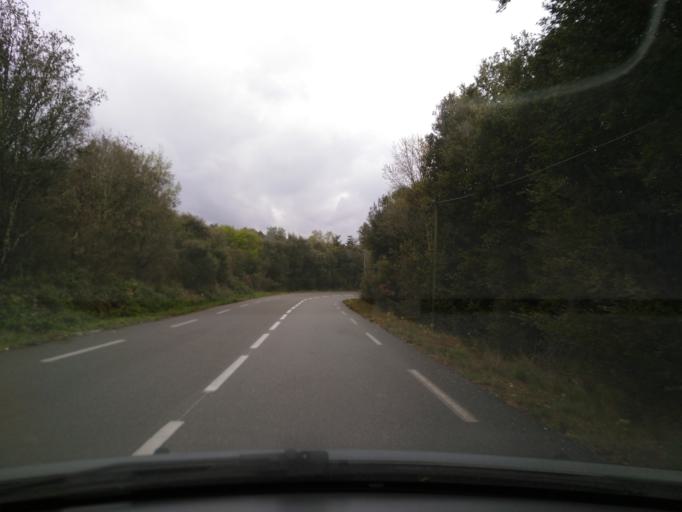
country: FR
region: Languedoc-Roussillon
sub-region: Departement du Gard
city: Barjac
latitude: 44.3451
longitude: 4.4100
